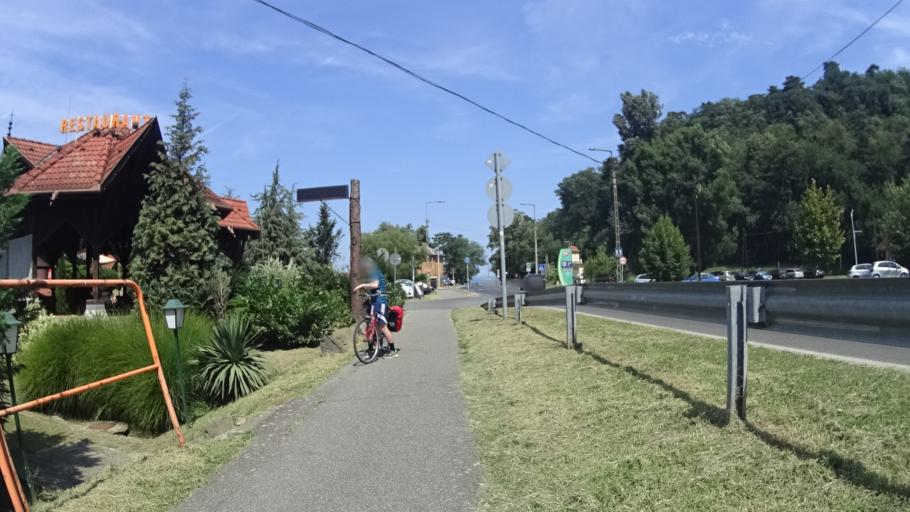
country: HU
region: Somogy
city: Balatonfenyves
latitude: 46.7363
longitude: 17.5349
